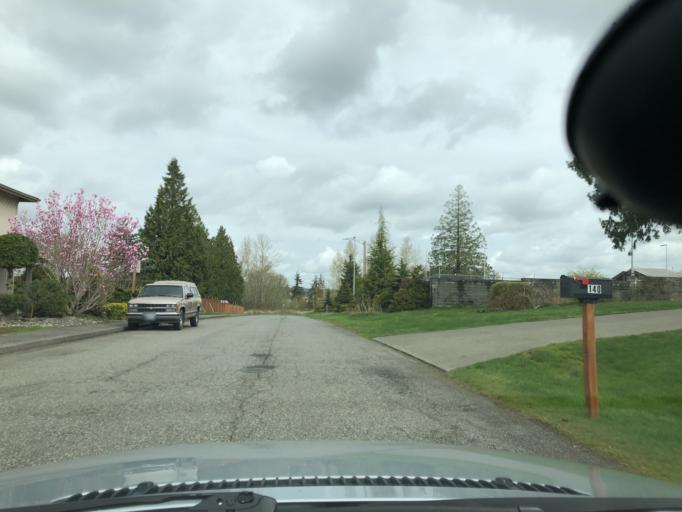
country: US
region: Washington
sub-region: Whatcom County
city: Blaine
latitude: 48.9999
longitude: -122.7401
